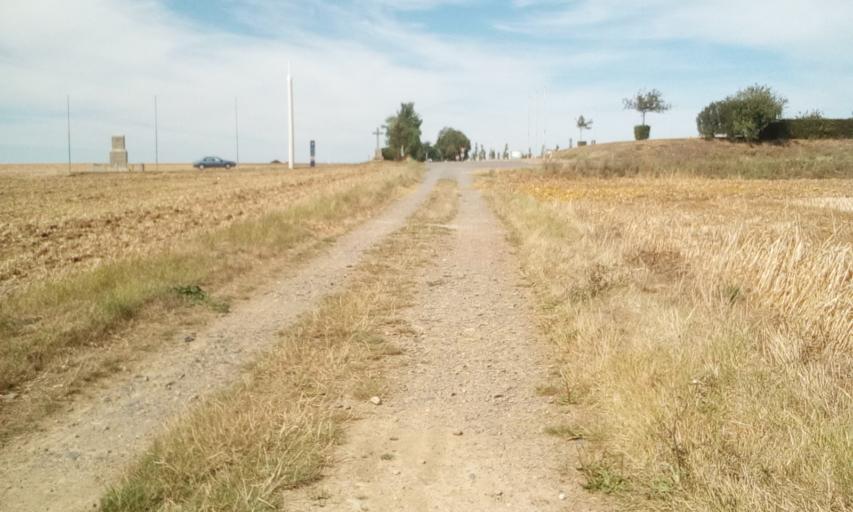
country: FR
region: Lower Normandy
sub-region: Departement du Calvados
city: Fontaine-Etoupefour
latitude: 49.1225
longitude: -0.4604
